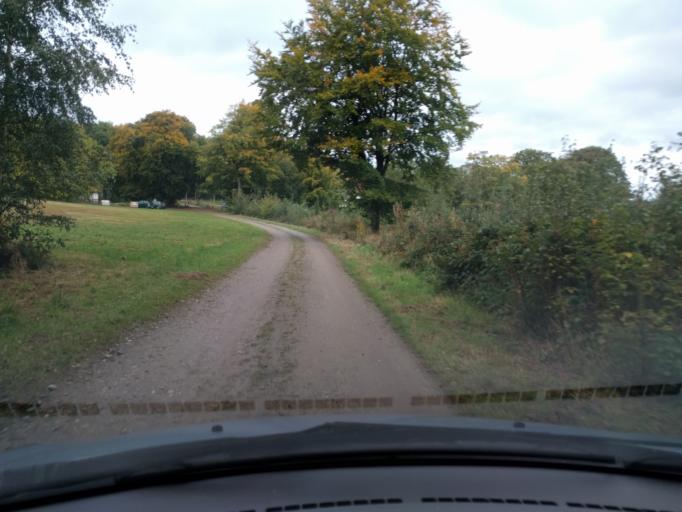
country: DK
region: South Denmark
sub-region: Kerteminde Kommune
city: Kerteminde
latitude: 55.4762
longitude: 10.6945
